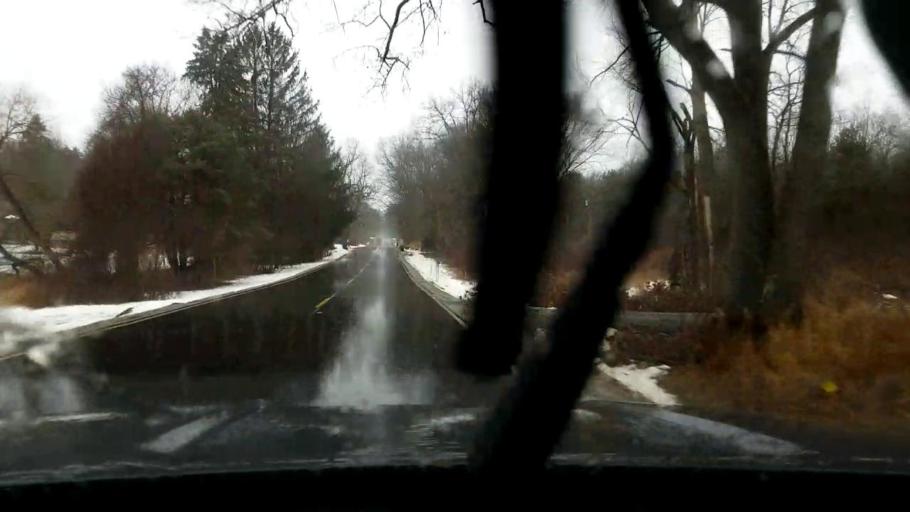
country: US
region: Michigan
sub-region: Jackson County
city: Grass Lake
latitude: 42.3363
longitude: -84.1681
